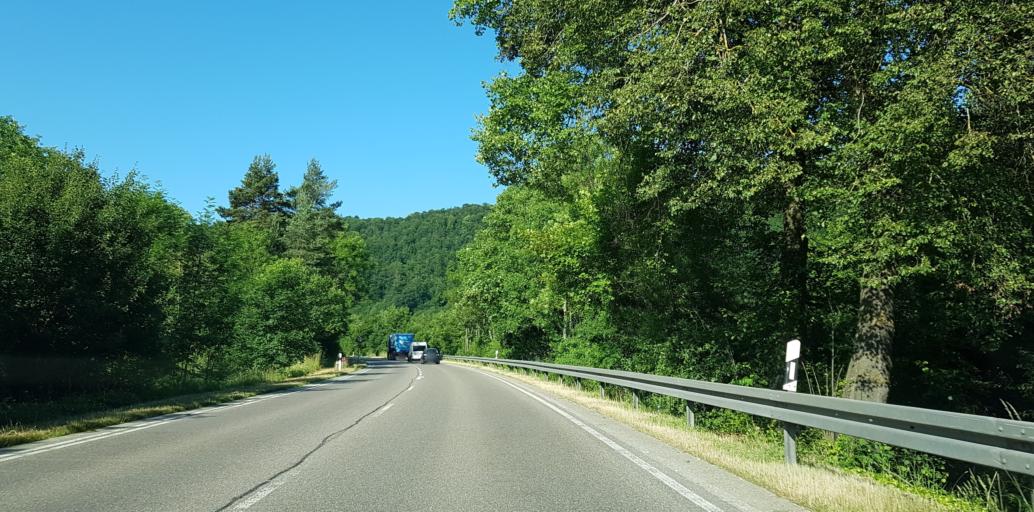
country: DE
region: Baden-Wuerttemberg
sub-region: Tuebingen Region
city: Blaubeuren
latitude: 48.4030
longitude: 9.7710
